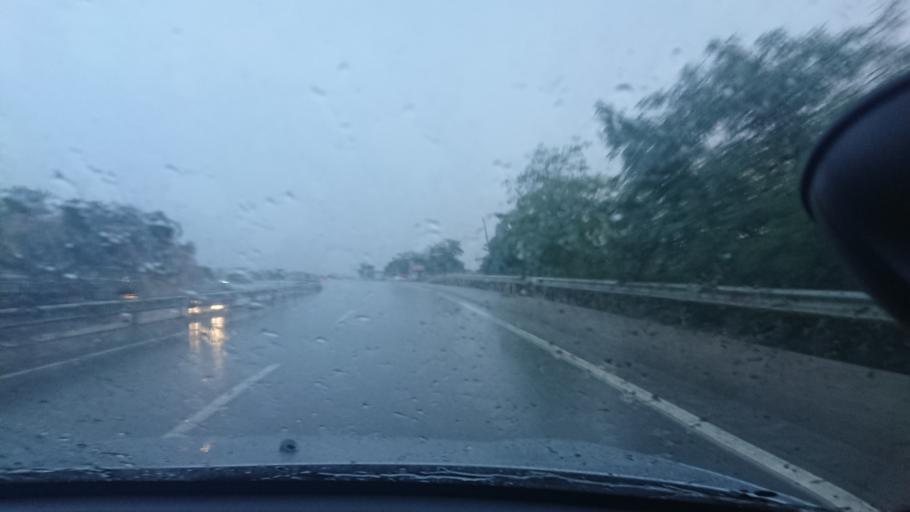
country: TR
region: Manisa
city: Adala
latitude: 38.5191
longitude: 28.3650
